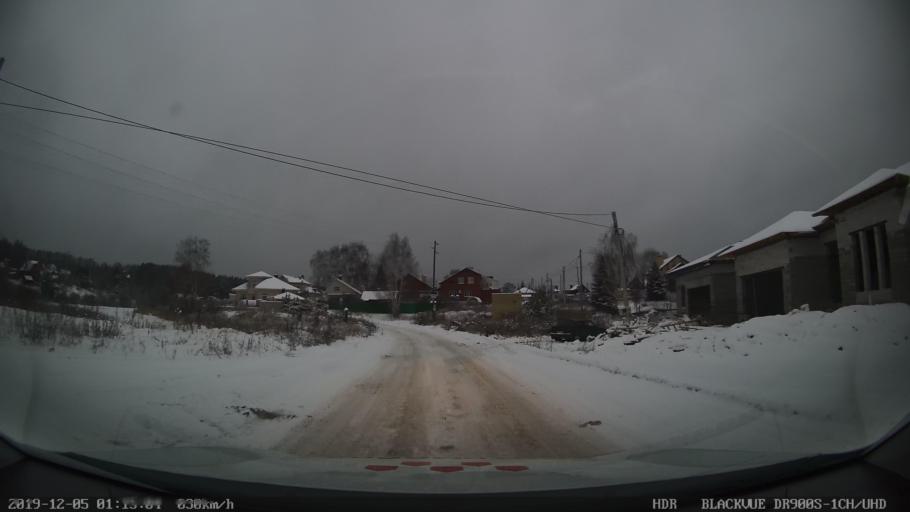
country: RU
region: Tatarstan
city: Stolbishchi
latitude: 55.6448
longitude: 49.1140
